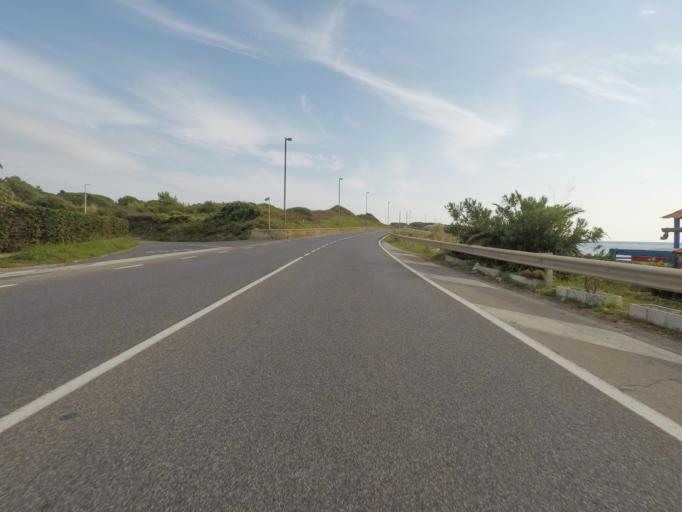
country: IT
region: Latium
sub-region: Citta metropolitana di Roma Capitale
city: Santa Marinella
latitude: 42.0381
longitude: 11.8323
